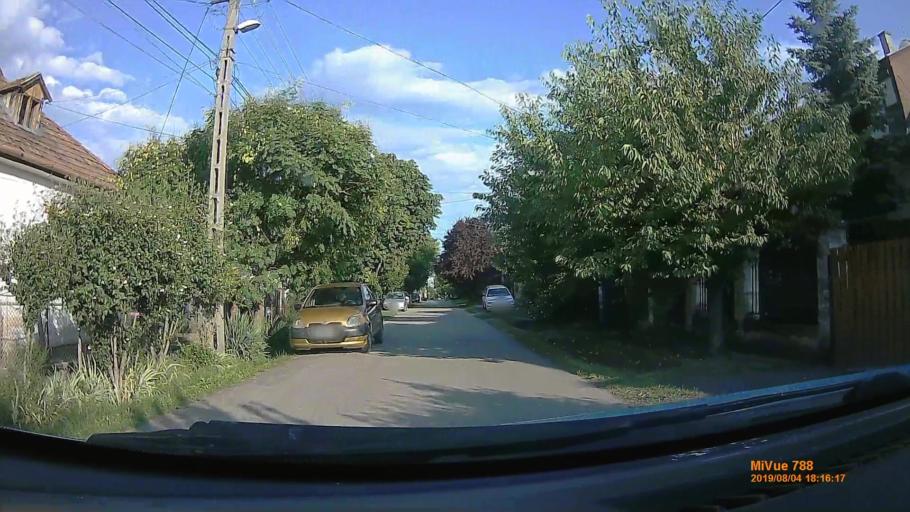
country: HU
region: Pest
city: God
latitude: 47.7029
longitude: 19.1516
